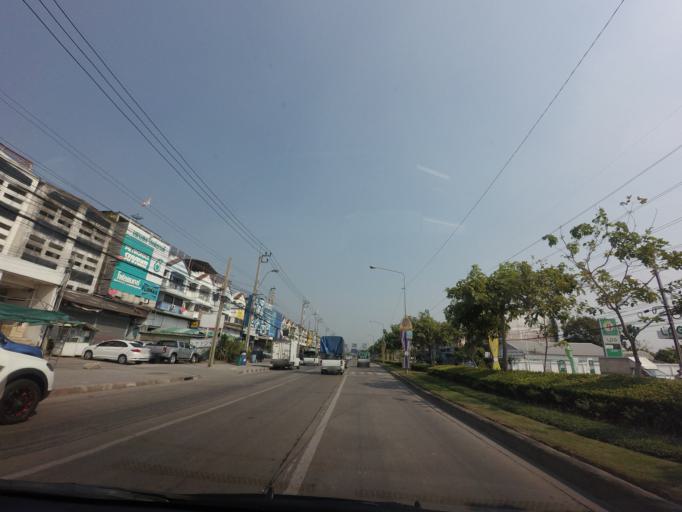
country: TH
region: Bangkok
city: Lat Krabang
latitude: 13.7511
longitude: 100.7898
